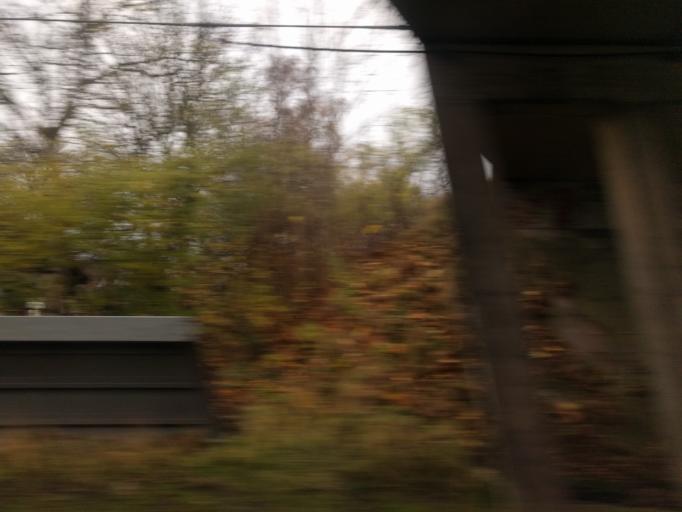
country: DK
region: Zealand
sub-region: Slagelse Kommune
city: Forlev
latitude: 55.3756
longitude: 11.2593
